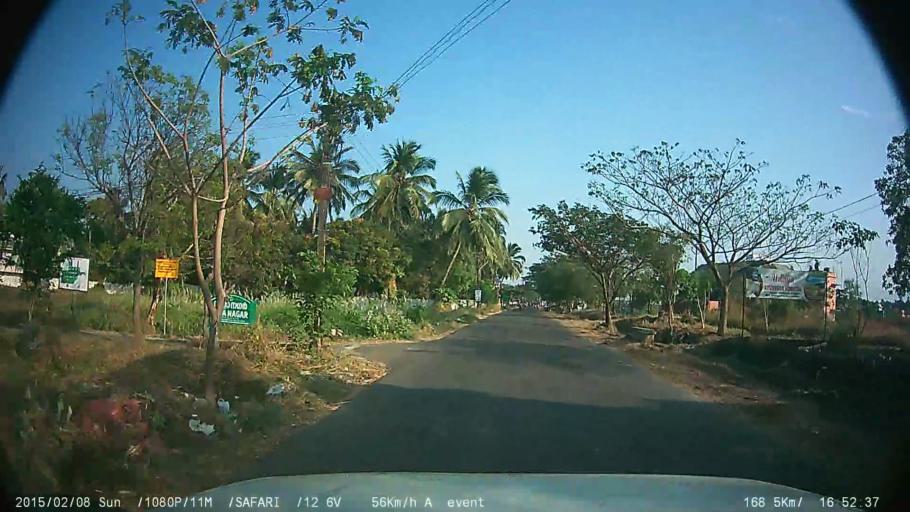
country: IN
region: Kerala
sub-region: Palakkad district
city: Palakkad
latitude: 10.7474
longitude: 76.6490
